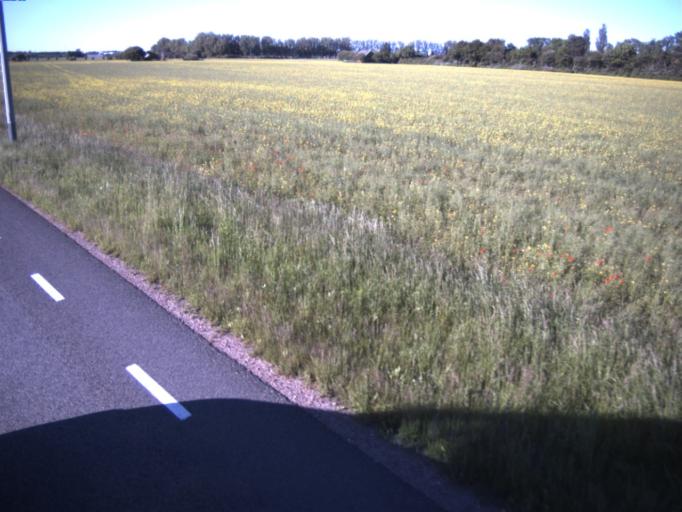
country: SE
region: Skane
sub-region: Helsingborg
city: Rydeback
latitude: 55.9836
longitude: 12.7691
